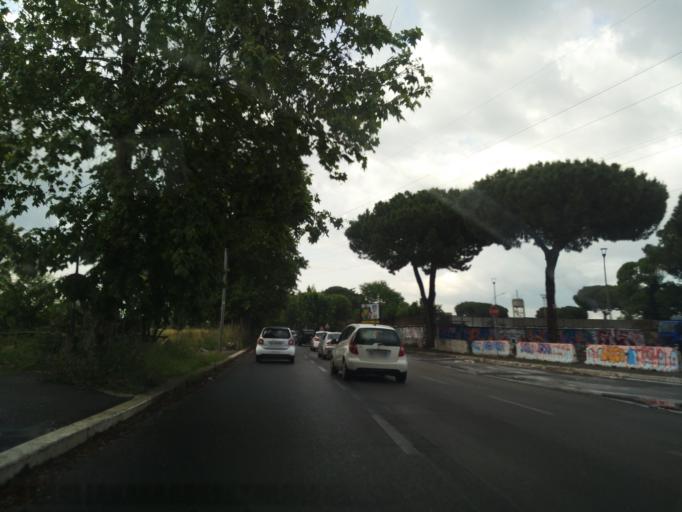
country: IT
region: Latium
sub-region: Citta metropolitana di Roma Capitale
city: Rome
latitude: 41.8972
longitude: 12.5758
